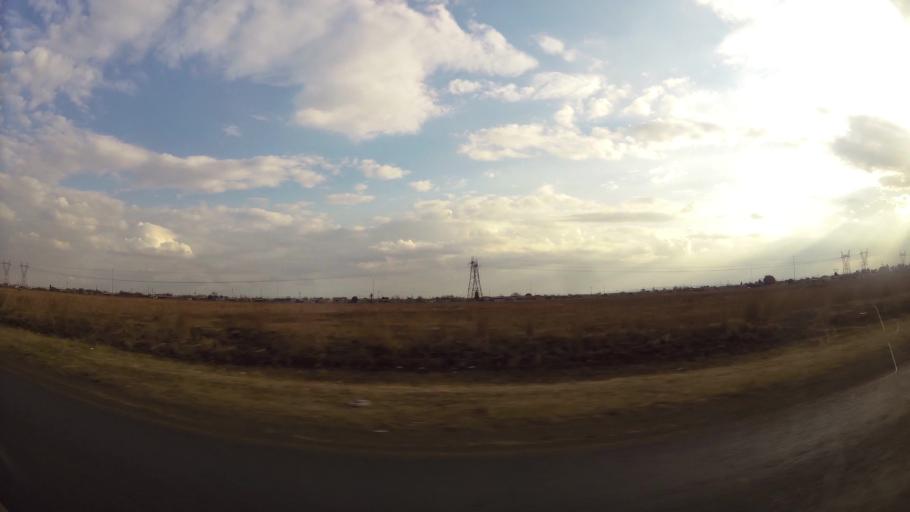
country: ZA
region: Gauteng
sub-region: Sedibeng District Municipality
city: Vanderbijlpark
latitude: -26.6788
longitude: 27.7945
